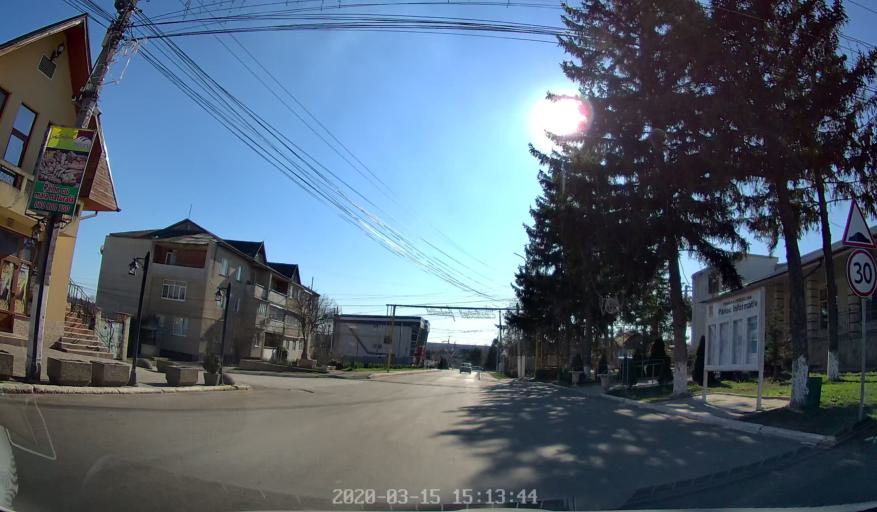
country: MD
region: Chisinau
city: Cricova
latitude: 47.2491
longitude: 28.7696
